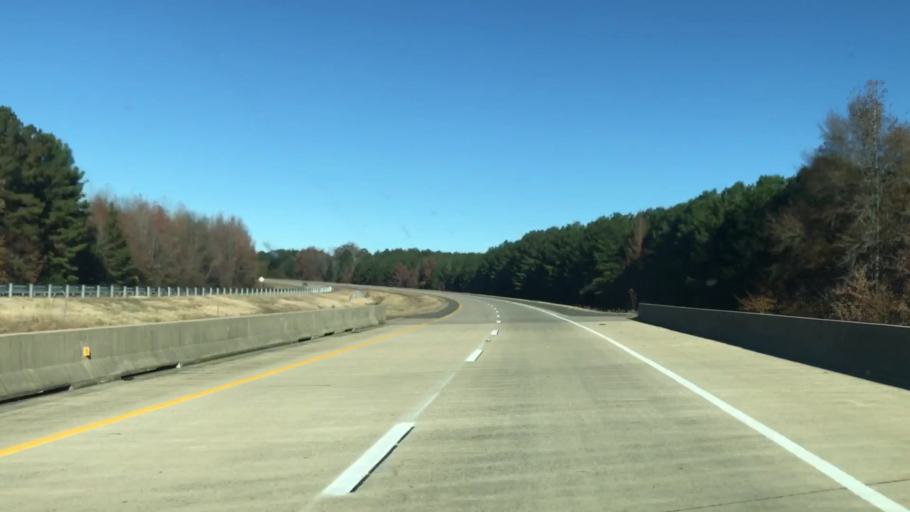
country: US
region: Texas
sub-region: Bowie County
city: Texarkana
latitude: 33.2407
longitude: -93.8734
